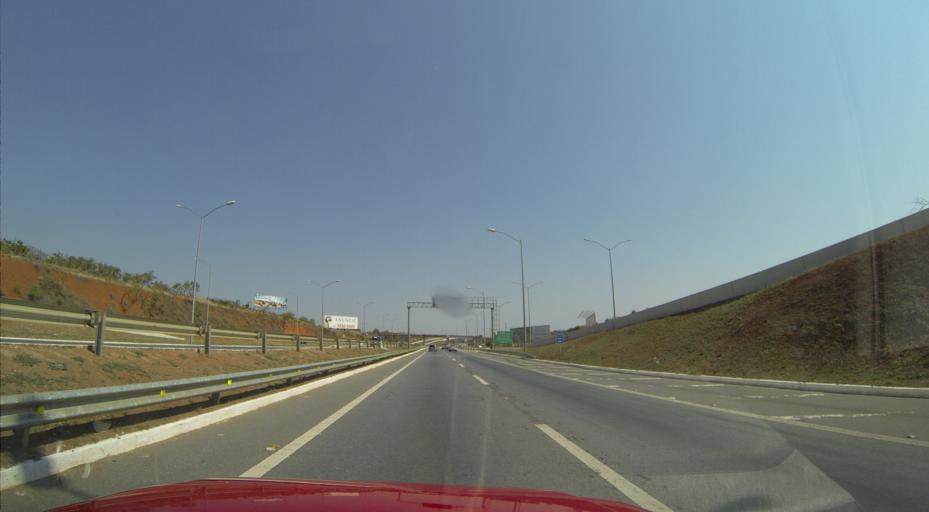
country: BR
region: Minas Gerais
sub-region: Vespasiano
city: Vespasiano
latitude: -19.6769
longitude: -43.9077
